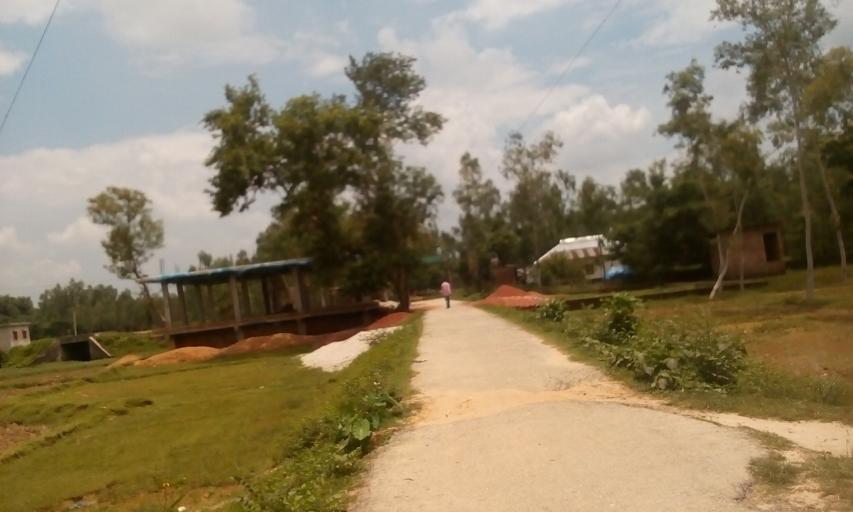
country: BD
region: Rangpur Division
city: Parbatipur
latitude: 25.4005
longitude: 88.9882
